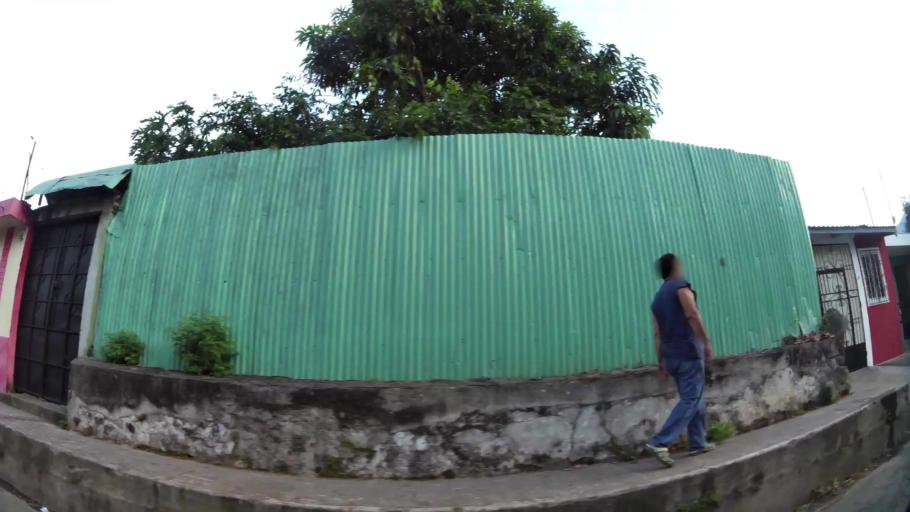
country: SV
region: San Vicente
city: San Vicente
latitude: 13.6465
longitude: -88.7874
